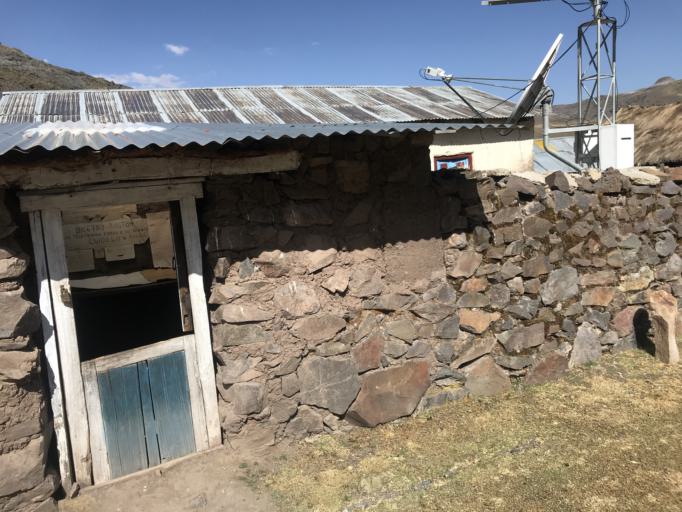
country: PE
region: Lima
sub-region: Provincia de Yauyos
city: Tupe
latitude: -12.6393
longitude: -75.7253
